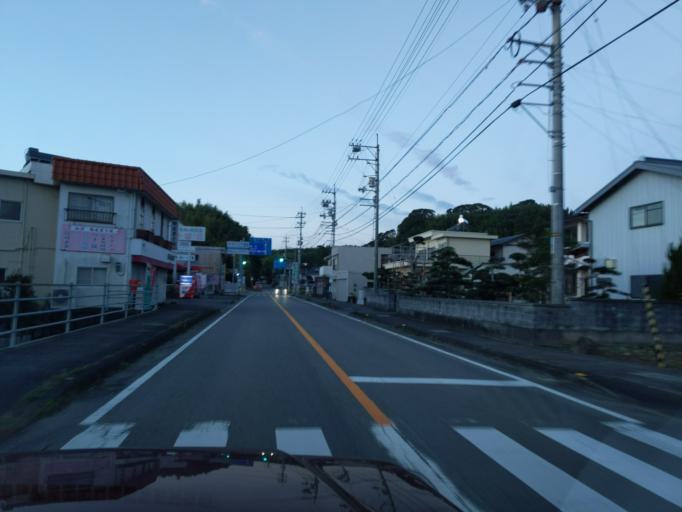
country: JP
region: Tokushima
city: Anan
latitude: 33.8422
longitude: 134.6237
